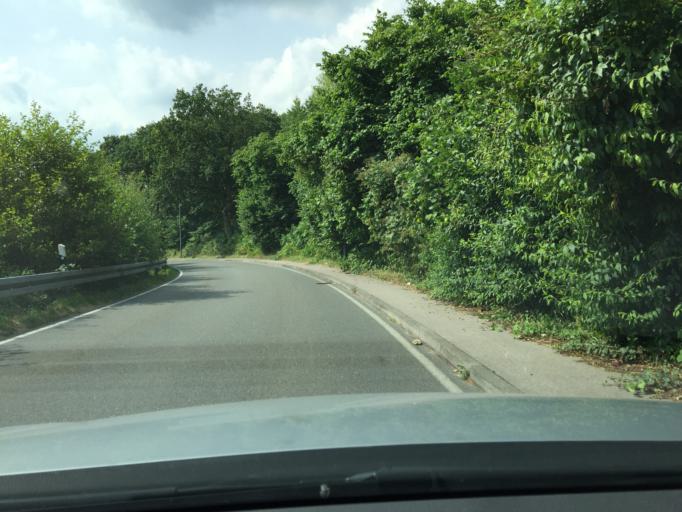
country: DE
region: North Rhine-Westphalia
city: Hattingen
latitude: 51.3667
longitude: 7.1189
